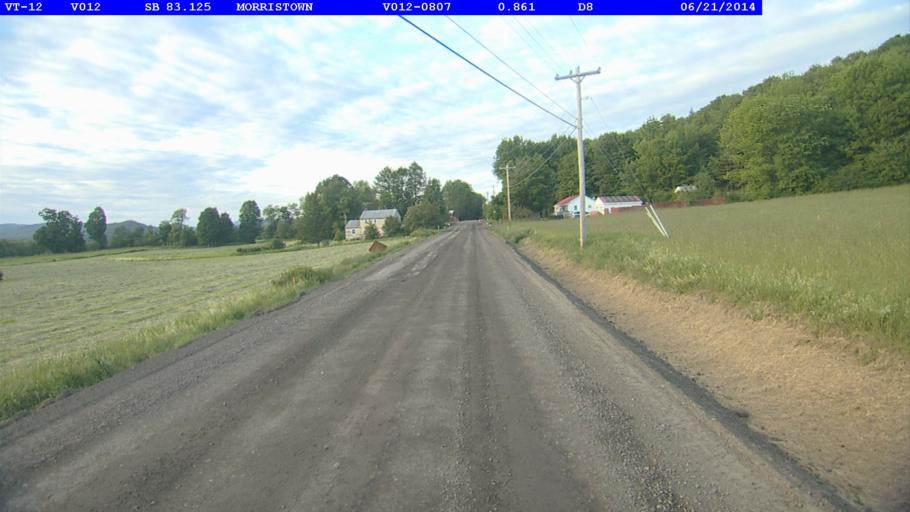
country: US
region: Vermont
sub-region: Lamoille County
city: Morrisville
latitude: 44.5497
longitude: -72.5552
